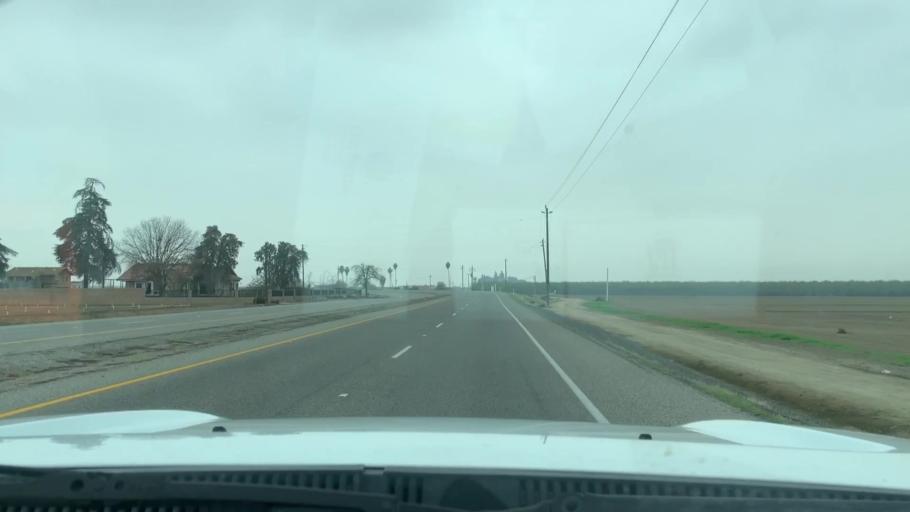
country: US
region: California
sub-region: Kern County
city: Wasco
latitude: 35.5499
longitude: -119.3321
